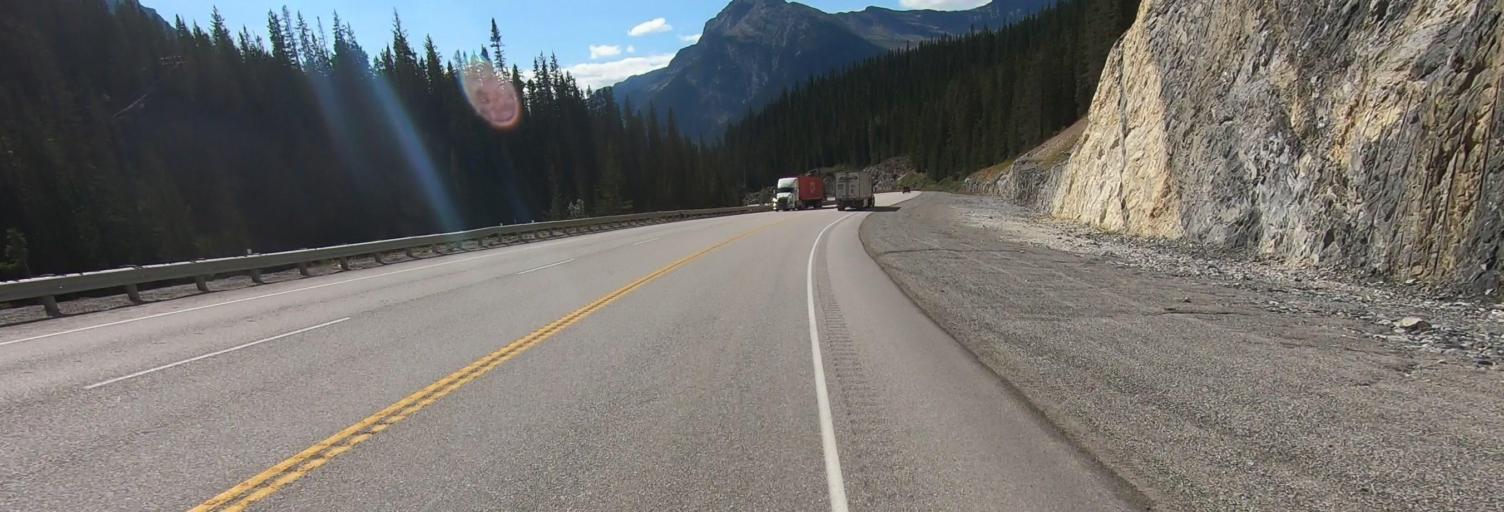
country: CA
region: Alberta
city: Lake Louise
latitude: 51.4371
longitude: -116.3813
